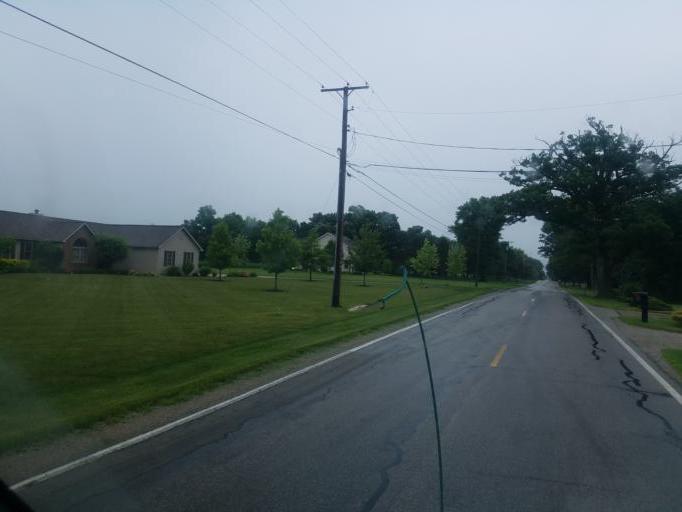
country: US
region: Ohio
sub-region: Marion County
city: Marion
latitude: 40.5495
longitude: -83.0911
